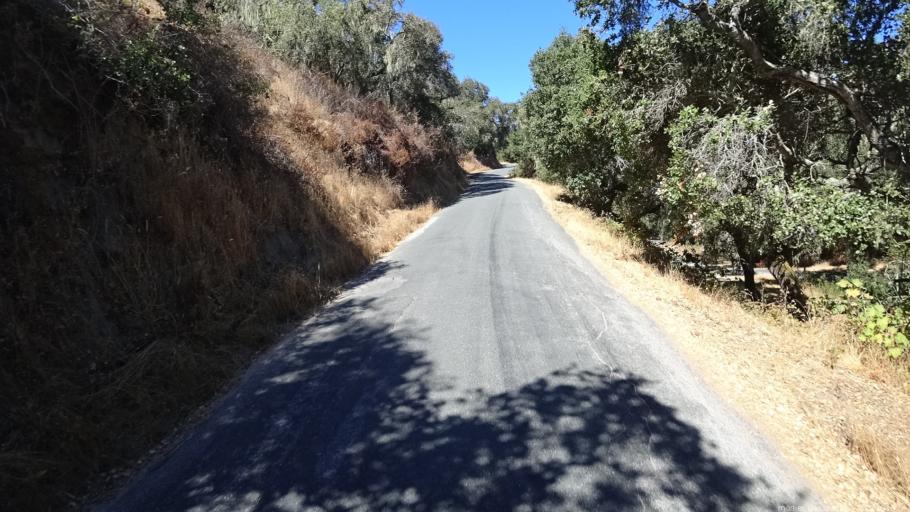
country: US
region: California
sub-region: Monterey County
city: Carmel Valley Village
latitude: 36.4830
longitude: -121.8046
